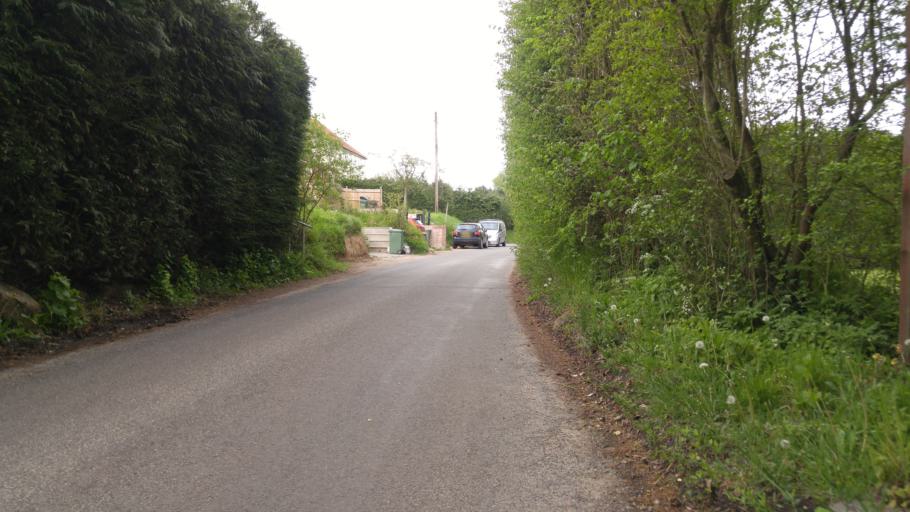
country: GB
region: England
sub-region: Suffolk
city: Sudbury
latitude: 51.9858
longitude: 0.7462
